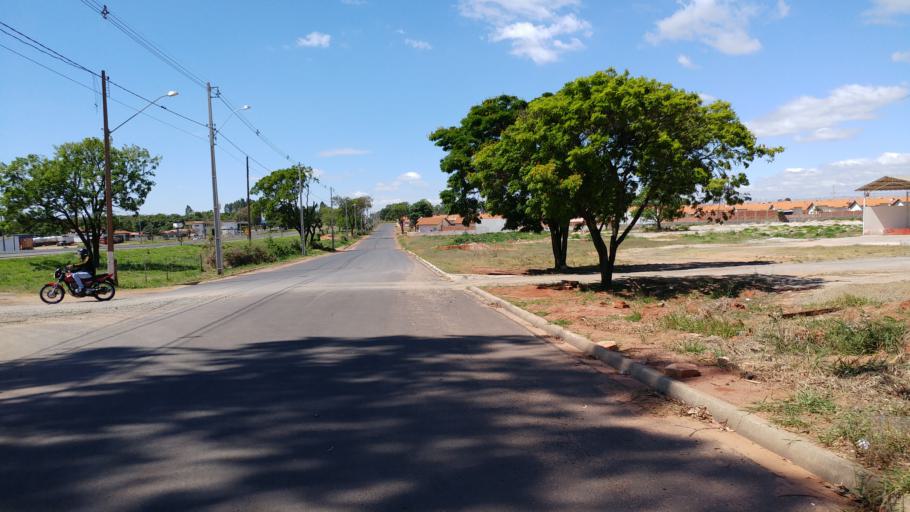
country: BR
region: Sao Paulo
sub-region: Paraguacu Paulista
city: Paraguacu Paulista
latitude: -22.4413
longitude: -50.5852
